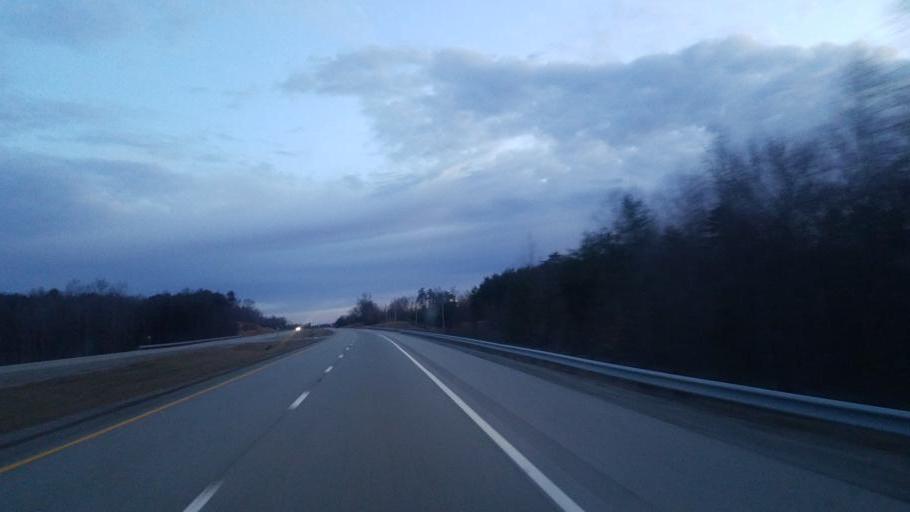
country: US
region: Tennessee
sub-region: Van Buren County
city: Spencer
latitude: 35.7041
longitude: -85.4770
